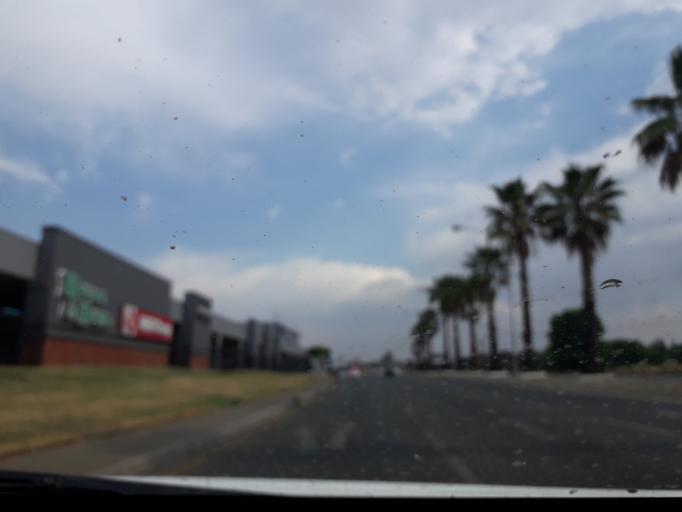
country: ZA
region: Gauteng
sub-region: City of Johannesburg Metropolitan Municipality
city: Modderfontein
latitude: -26.1031
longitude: 28.2212
